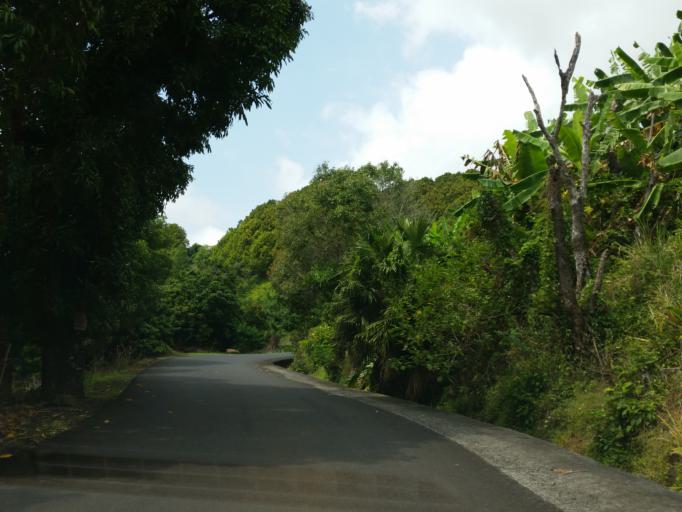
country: RE
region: Reunion
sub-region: Reunion
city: Sainte-Suzanne
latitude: -20.9262
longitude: 55.6058
